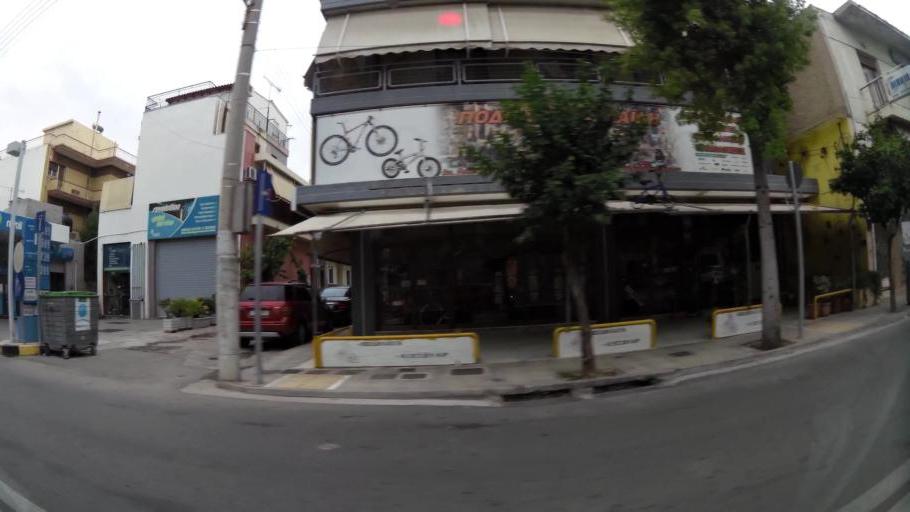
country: GR
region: Attica
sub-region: Nomarchia Athinas
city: Ilion
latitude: 38.0224
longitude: 23.7104
